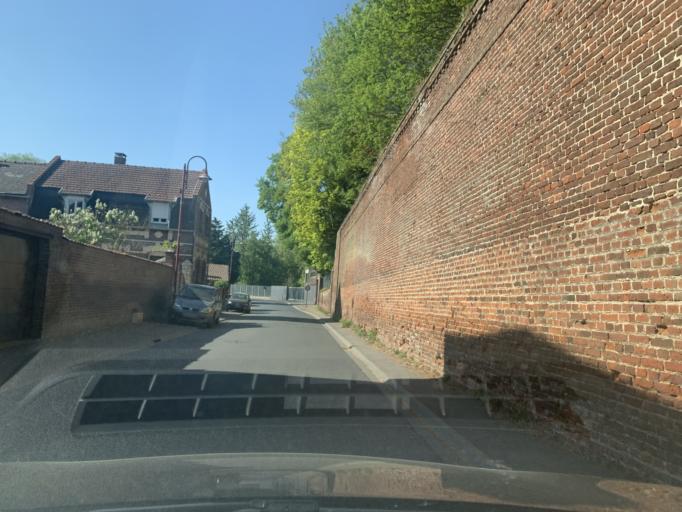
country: FR
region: Nord-Pas-de-Calais
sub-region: Departement du Nord
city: Proville
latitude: 50.1636
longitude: 3.2094
